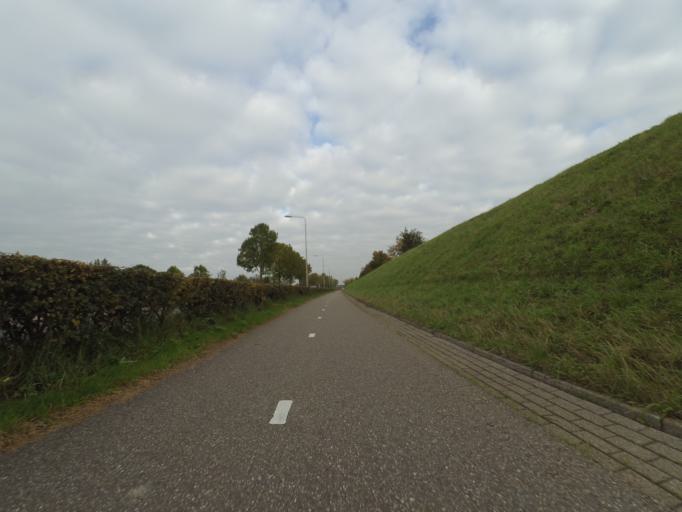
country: NL
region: Gelderland
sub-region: Gemeente Nijkerk
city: Nijkerk
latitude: 52.2237
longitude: 5.4709
